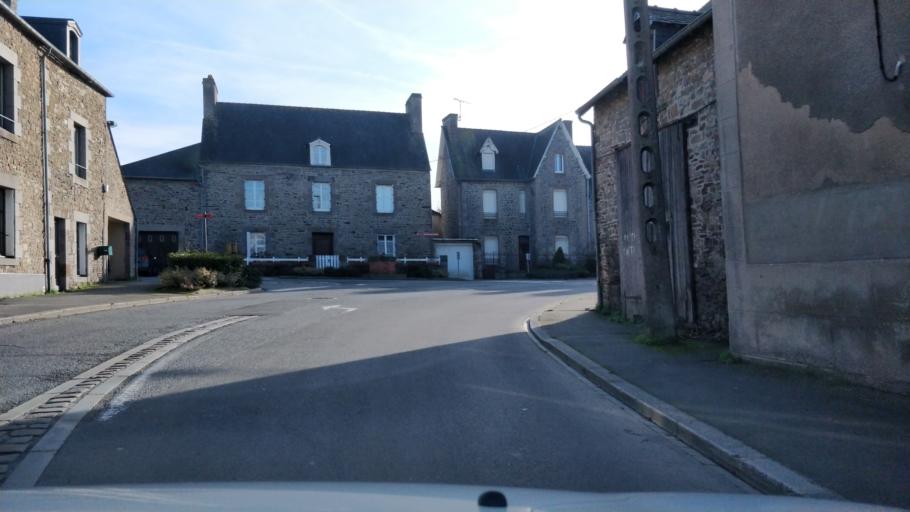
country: FR
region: Brittany
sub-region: Departement d'Ille-et-Vilaine
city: Dol-de-Bretagne
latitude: 48.5430
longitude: -1.7599
